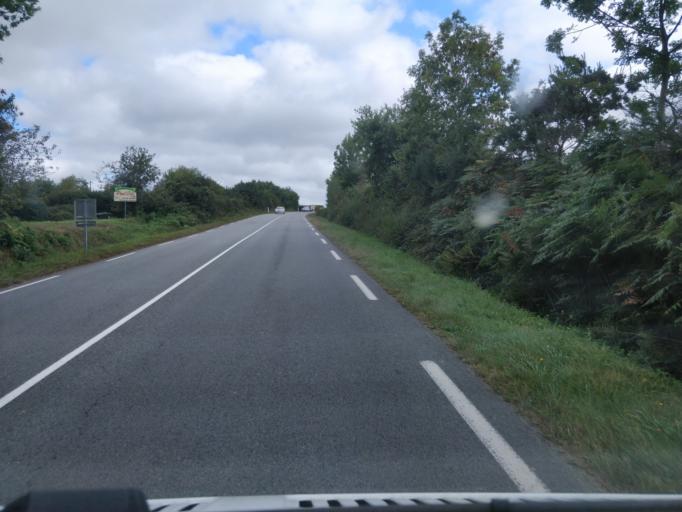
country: FR
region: Brittany
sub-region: Departement du Finistere
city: Pluguffan
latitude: 47.9970
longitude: -4.1987
